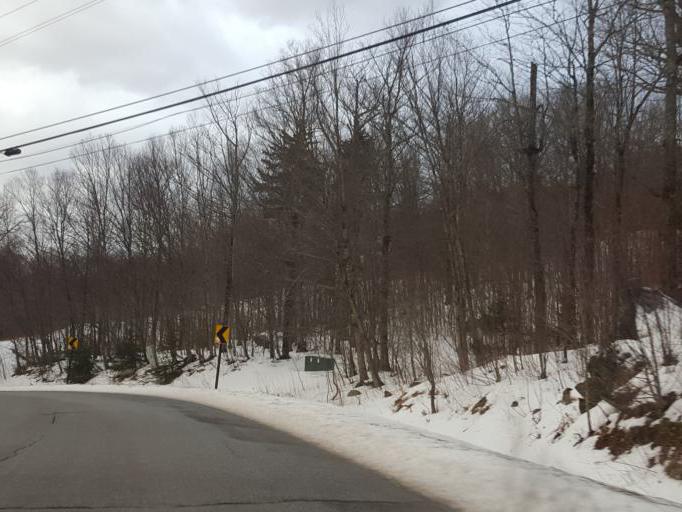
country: US
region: Vermont
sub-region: Rutland County
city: Rutland
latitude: 43.6307
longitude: -72.7782
